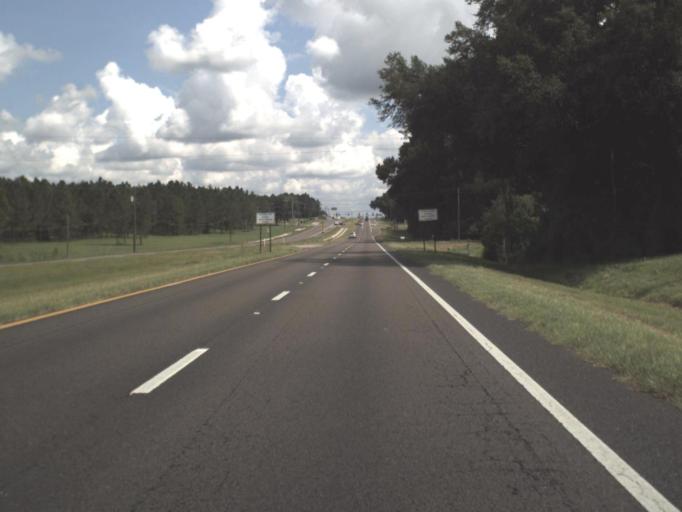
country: US
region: Florida
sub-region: Pasco County
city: Dade City
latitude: 28.3197
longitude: -82.1875
